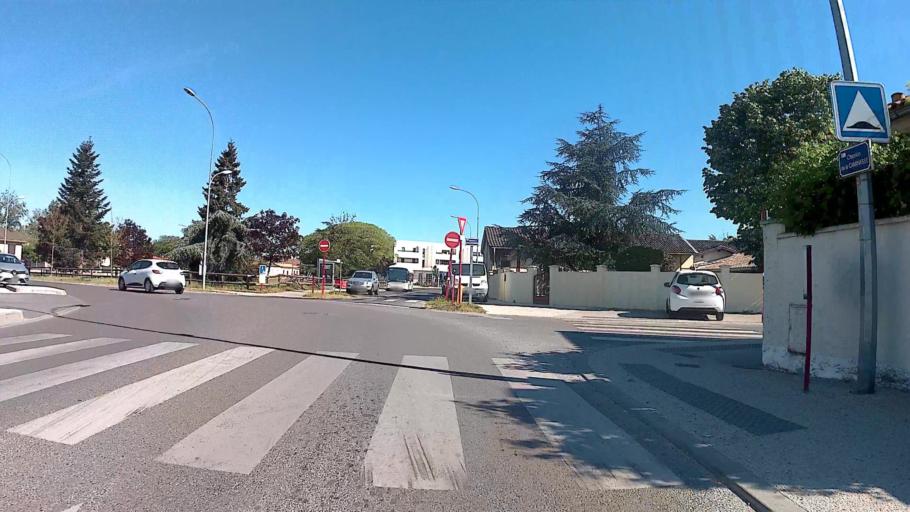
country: FR
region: Aquitaine
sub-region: Departement de la Gironde
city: Villenave-d'Ornon
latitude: 44.7729
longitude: -0.5278
